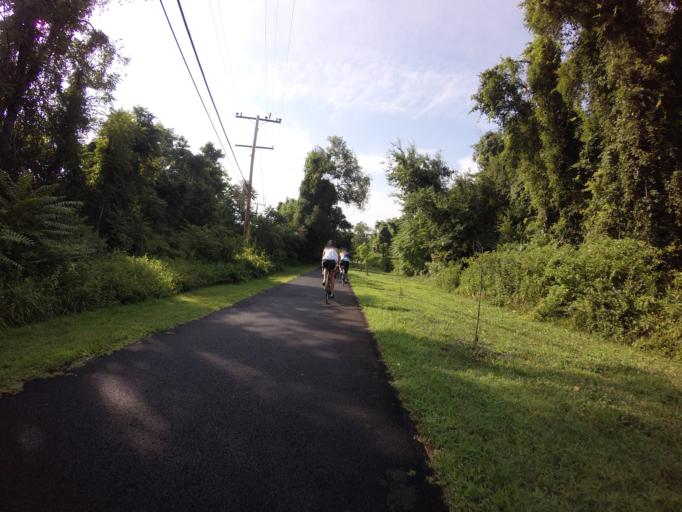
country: US
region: Maryland
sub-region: Anne Arundel County
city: Pasadena
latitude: 39.1224
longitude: -76.5906
